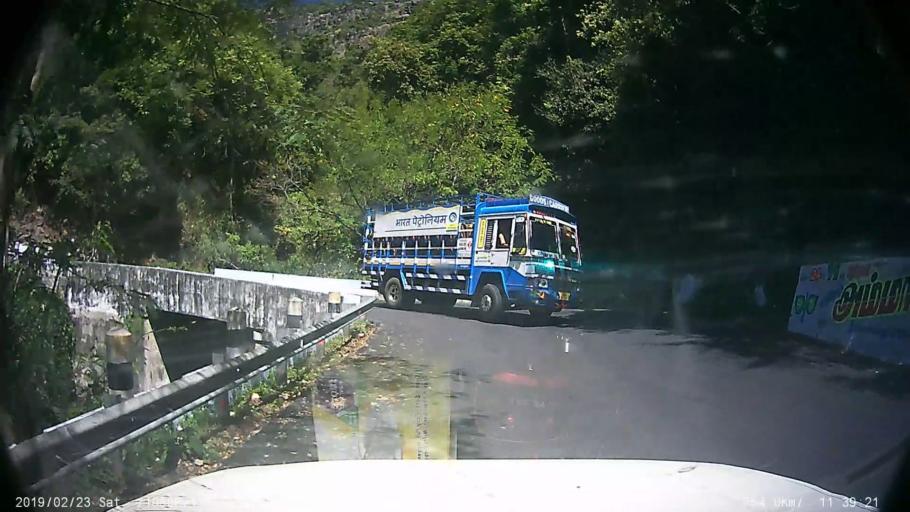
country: IN
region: Tamil Nadu
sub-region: Nilgiri
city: Wellington
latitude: 11.3400
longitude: 76.8417
